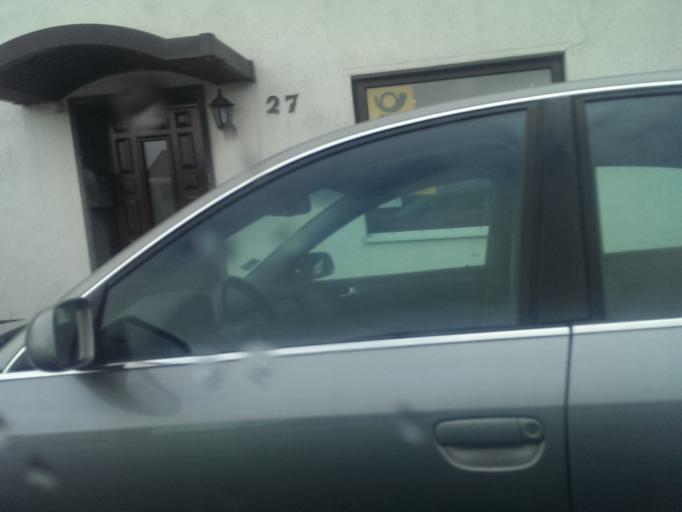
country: DE
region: Lower Saxony
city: Schellerten
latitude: 52.1521
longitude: 10.0885
